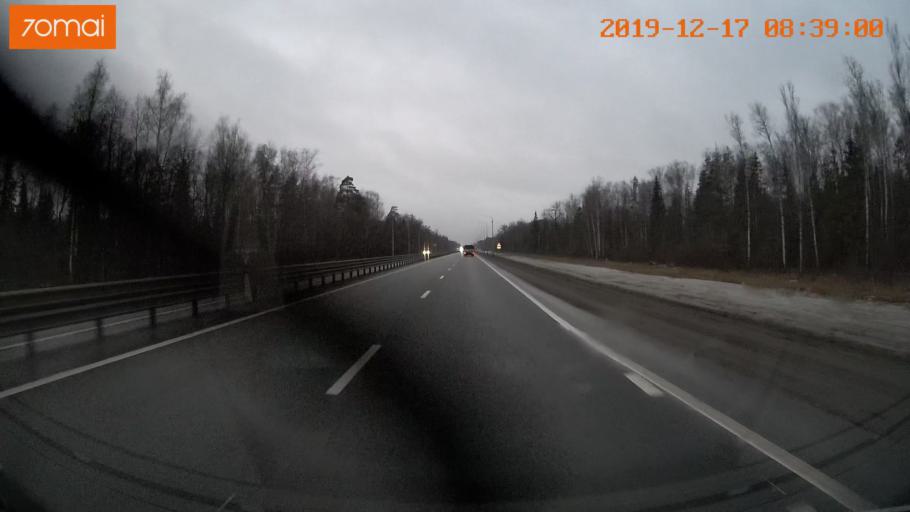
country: RU
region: Vladimir
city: Lakinsk
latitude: 55.9771
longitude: 39.8205
